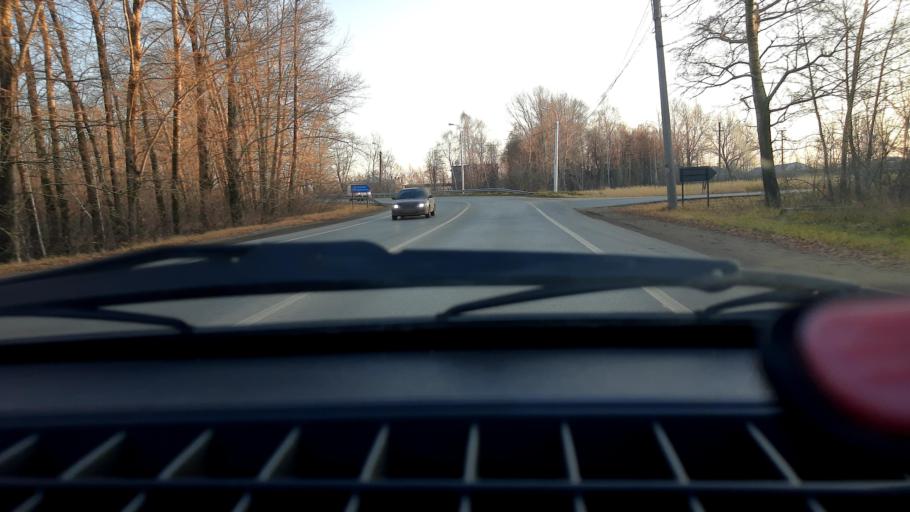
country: RU
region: Bashkortostan
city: Blagoveshchensk
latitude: 54.9168
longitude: 56.0779
